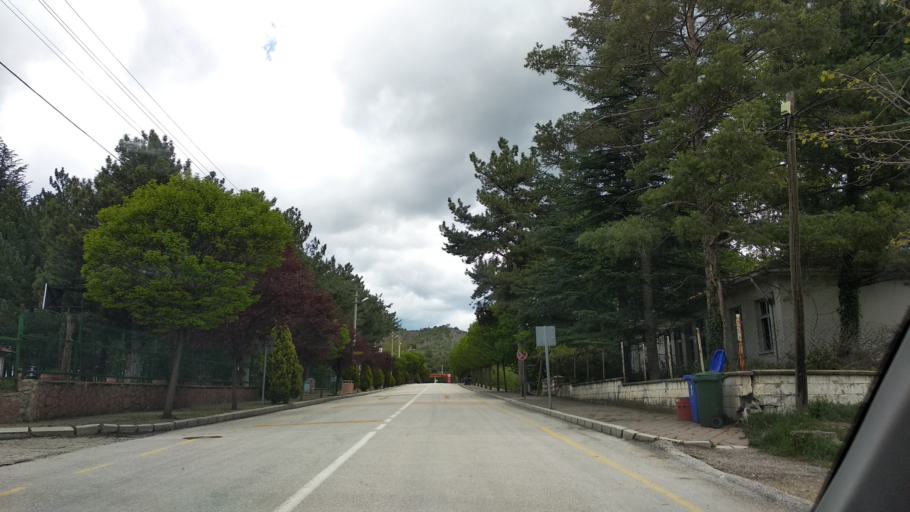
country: TR
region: Bolu
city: Seben
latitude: 40.4135
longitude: 31.5747
